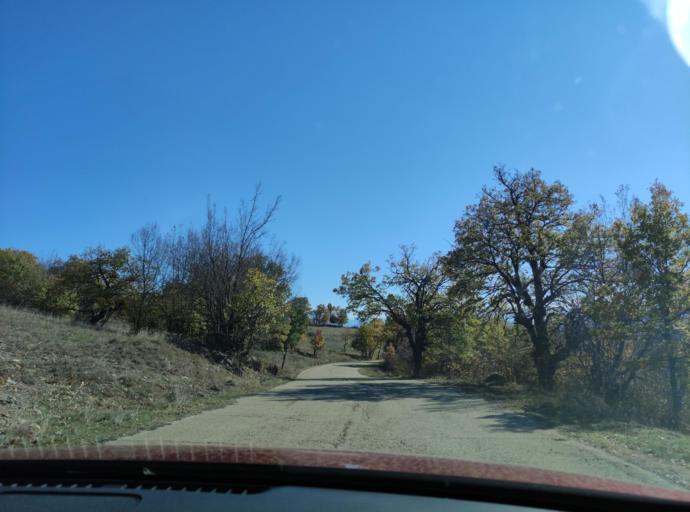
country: BG
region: Montana
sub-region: Obshtina Chiprovtsi
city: Chiprovtsi
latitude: 43.4482
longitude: 23.0467
